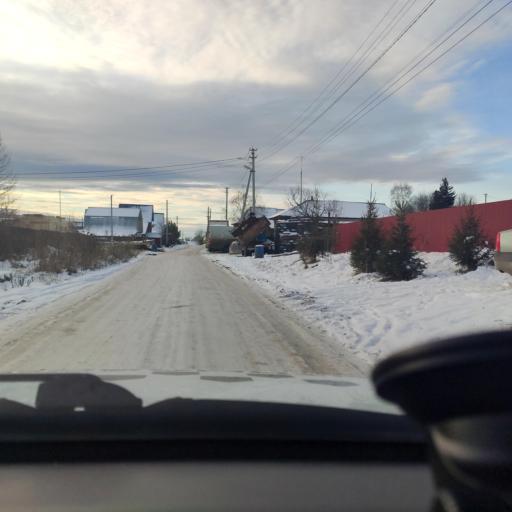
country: RU
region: Perm
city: Ferma
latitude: 57.9384
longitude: 56.3466
